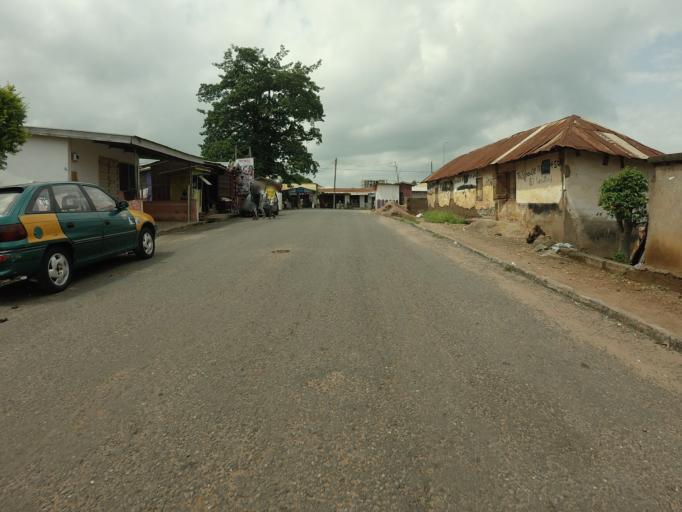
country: GH
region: Volta
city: Ho
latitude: 6.6160
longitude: 0.4692
